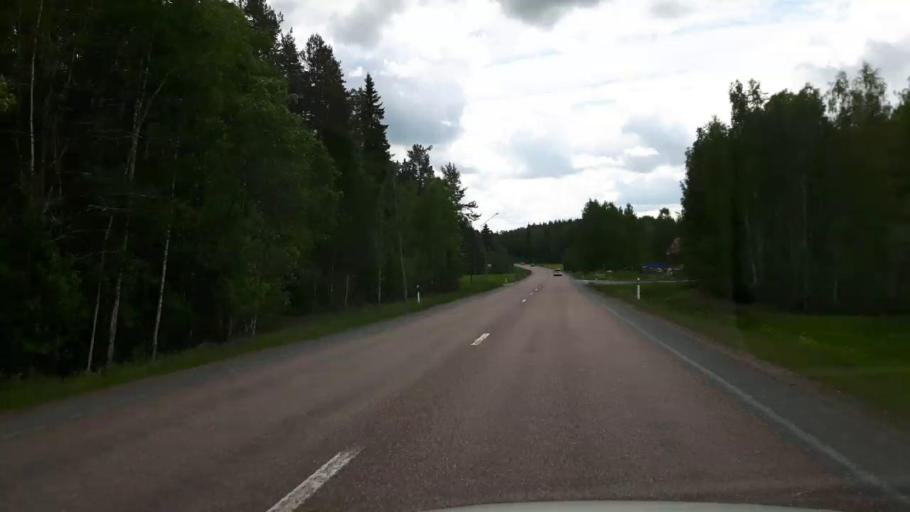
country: SE
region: Dalarna
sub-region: Faluns Kommun
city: Falun
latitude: 60.5111
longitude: 15.7368
